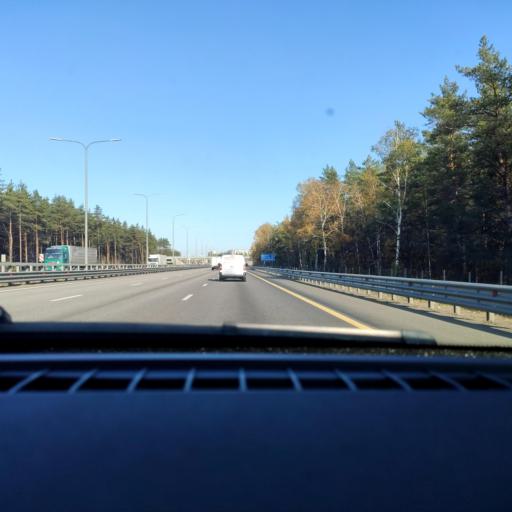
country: RU
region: Voronezj
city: Somovo
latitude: 51.7221
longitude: 39.3104
